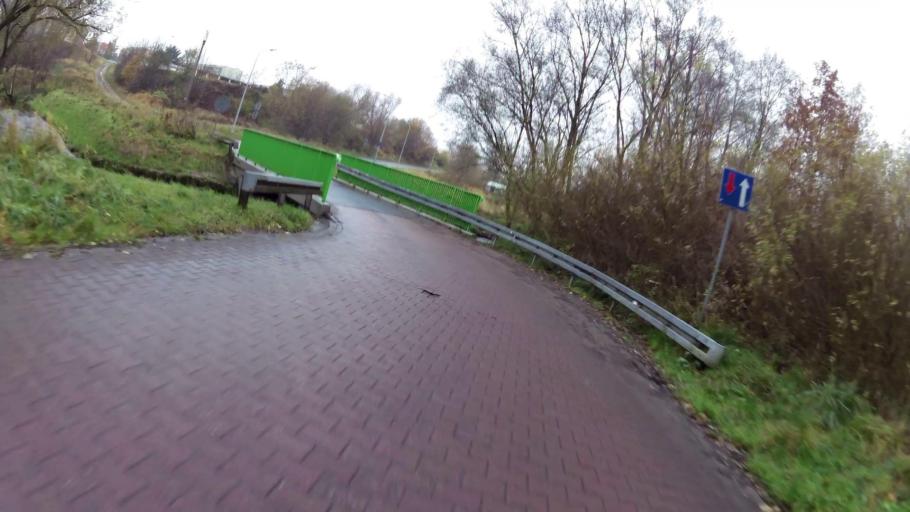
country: PL
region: West Pomeranian Voivodeship
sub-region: Koszalin
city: Koszalin
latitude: 54.2086
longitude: 16.1705
